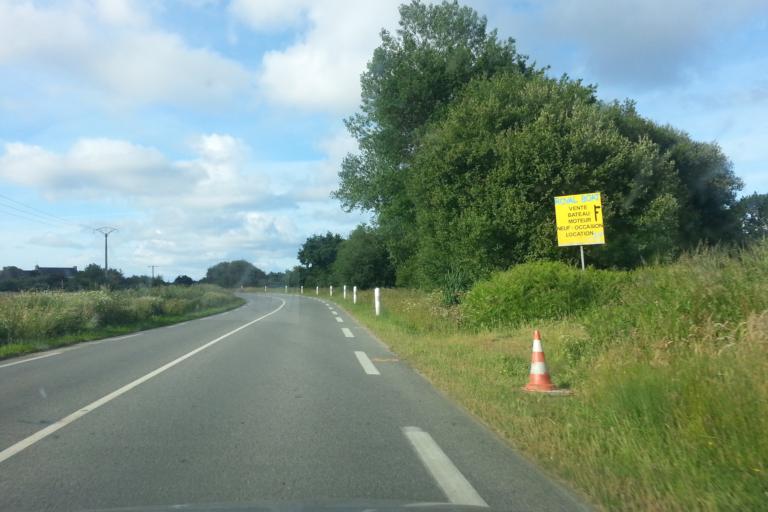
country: FR
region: Brittany
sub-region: Departement du Morbihan
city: Sainte-Helene
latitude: 47.6975
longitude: -3.2160
